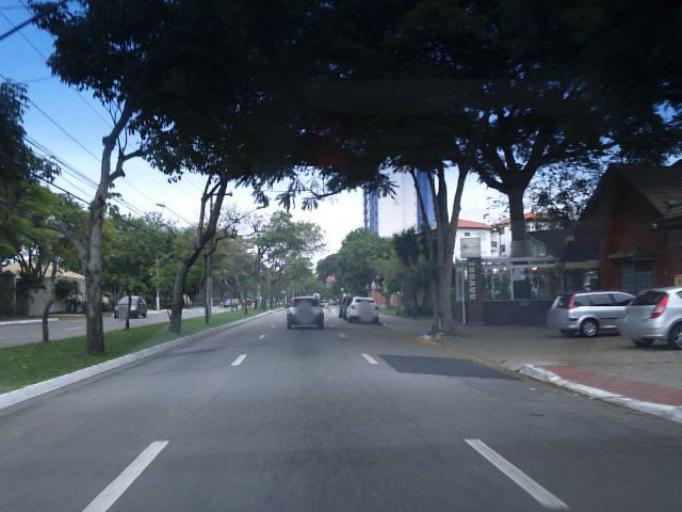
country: BR
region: Sao Paulo
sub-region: Sao Jose Dos Campos
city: Sao Jose dos Campos
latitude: -23.2412
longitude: -45.8817
